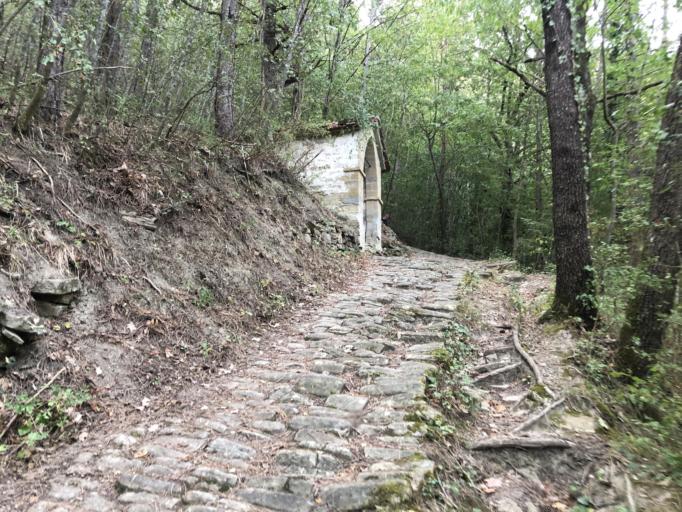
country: IT
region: Emilia-Romagna
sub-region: Forli-Cesena
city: Portico e San Benedetto
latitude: 44.0232
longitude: 11.7820
